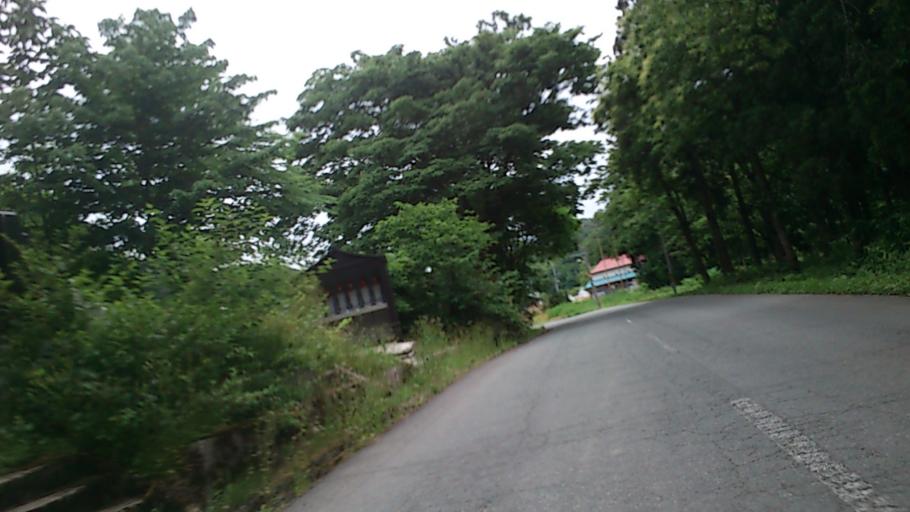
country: JP
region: Yamagata
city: Shinjo
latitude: 38.7127
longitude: 140.2690
